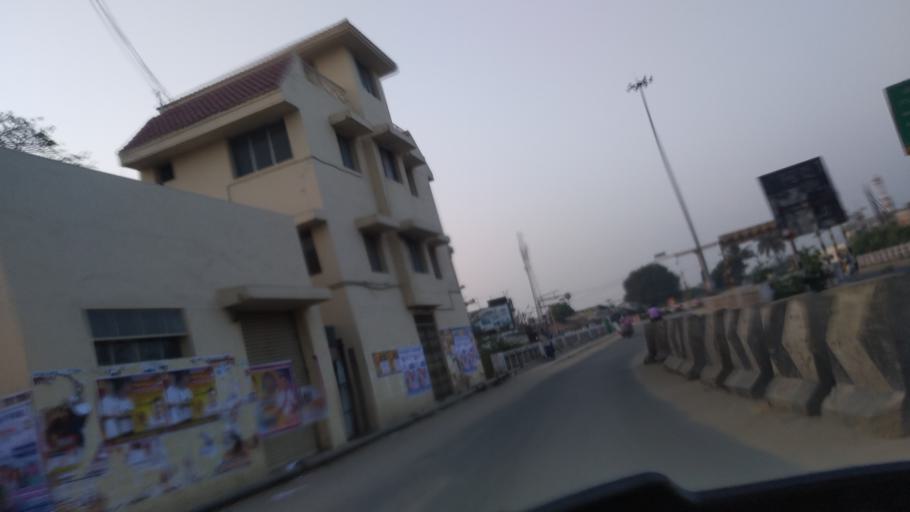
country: IN
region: Tamil Nadu
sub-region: Coimbatore
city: Coimbatore
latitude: 10.9757
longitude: 76.9620
